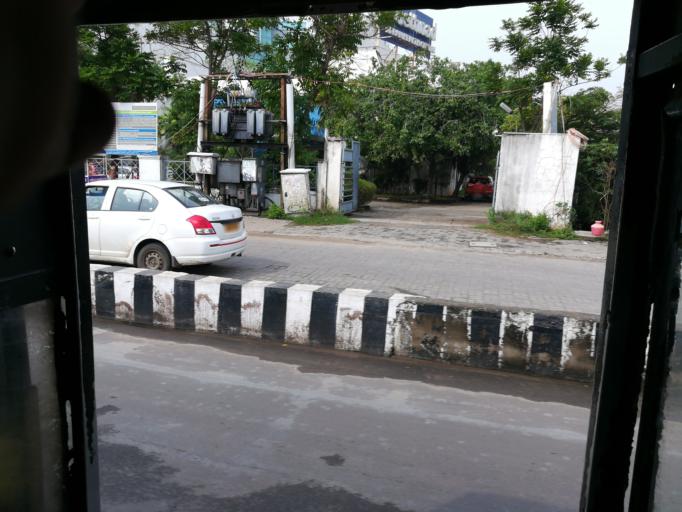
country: IN
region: Tamil Nadu
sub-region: Kancheepuram
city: Injambakkam
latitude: 12.9109
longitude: 80.2288
